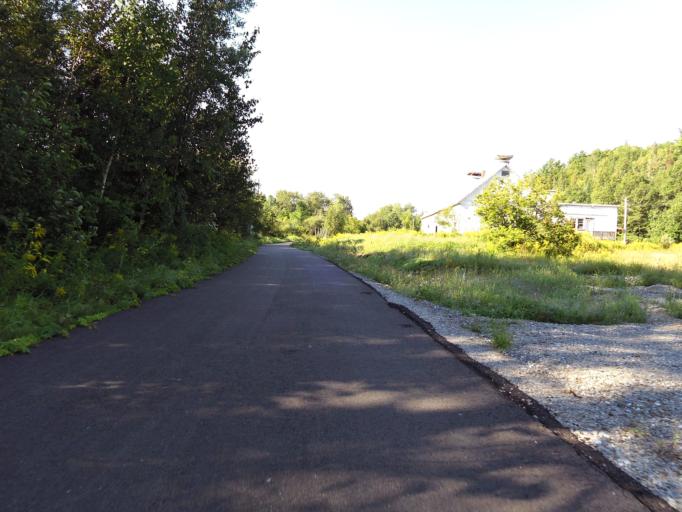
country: CA
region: Quebec
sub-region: Outaouais
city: Maniwaki
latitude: 46.2413
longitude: -76.0234
